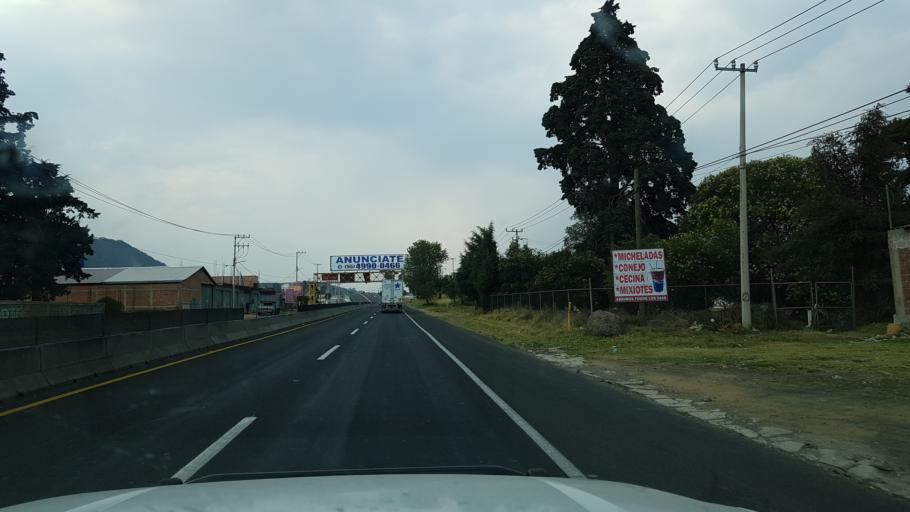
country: MX
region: Mexico
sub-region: Tlalmanalco
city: Santo Tomas Atzingo
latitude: 19.1612
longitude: -98.7807
